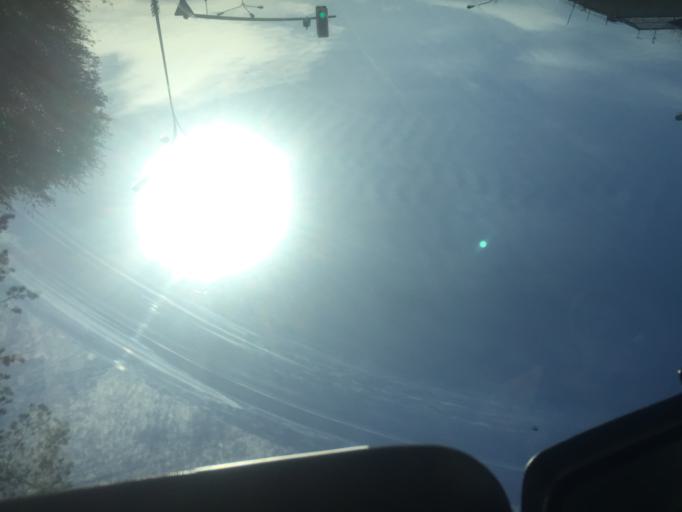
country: KZ
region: Astana Qalasy
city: Astana
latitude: 51.1642
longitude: 71.4144
